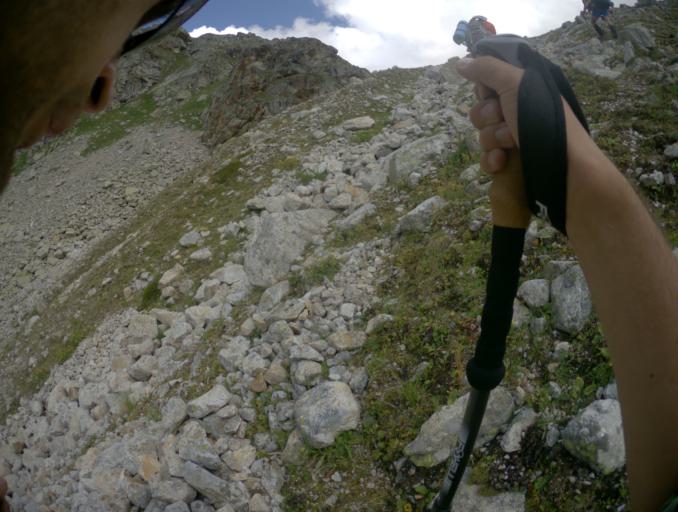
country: RU
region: Karachayevo-Cherkesiya
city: Uchkulan
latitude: 43.2839
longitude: 42.0950
